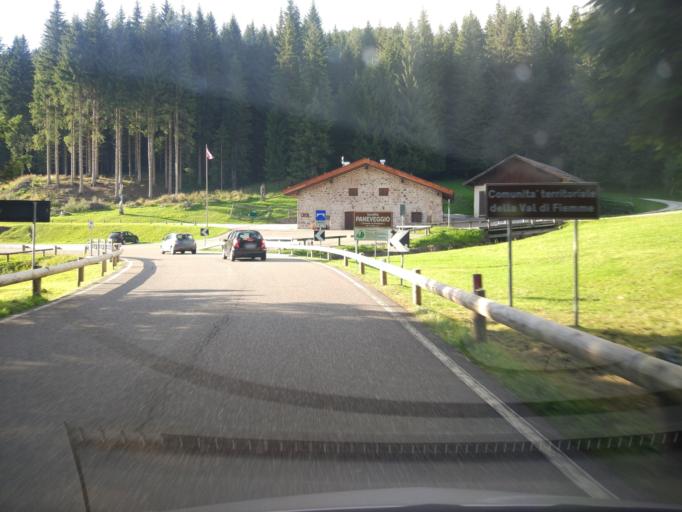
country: IT
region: Trentino-Alto Adige
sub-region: Provincia di Trento
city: Moena
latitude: 46.3094
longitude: 11.7488
